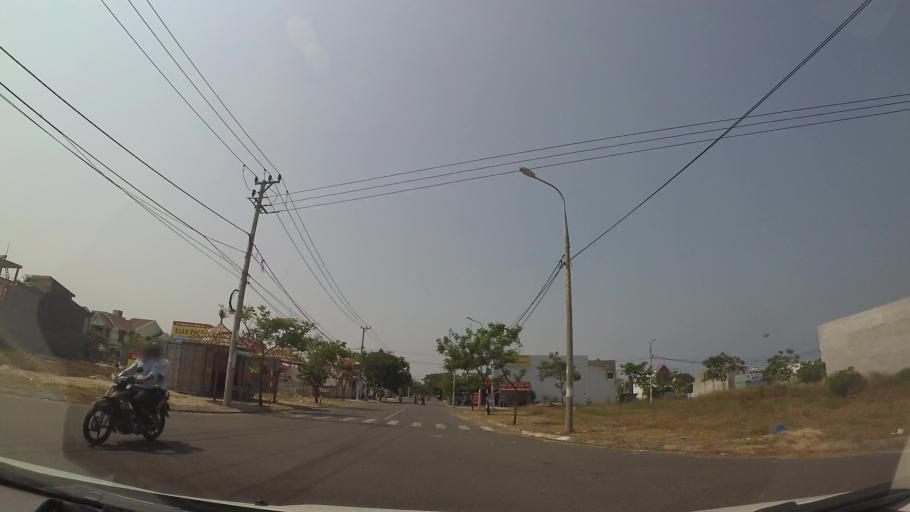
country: VN
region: Da Nang
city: Ngu Hanh Son
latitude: 15.9859
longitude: 108.2702
